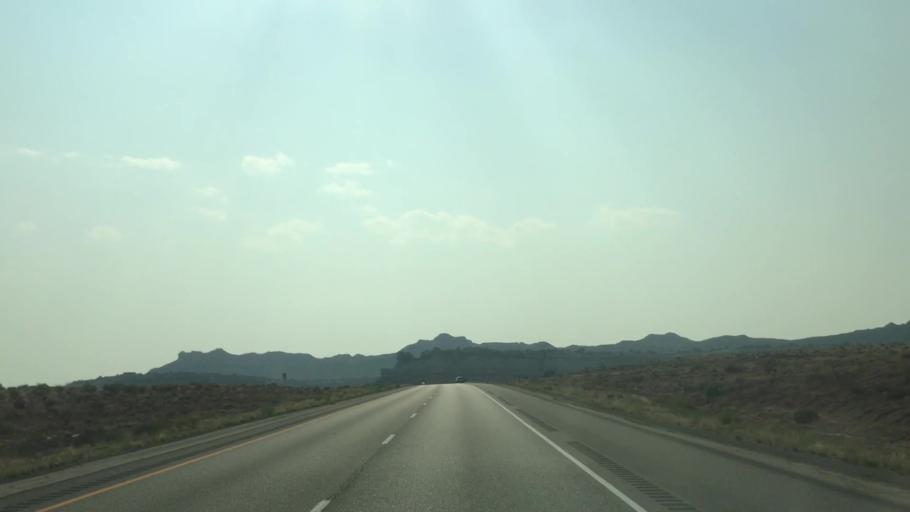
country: US
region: Utah
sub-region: Emery County
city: Ferron
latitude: 38.8405
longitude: -111.0899
